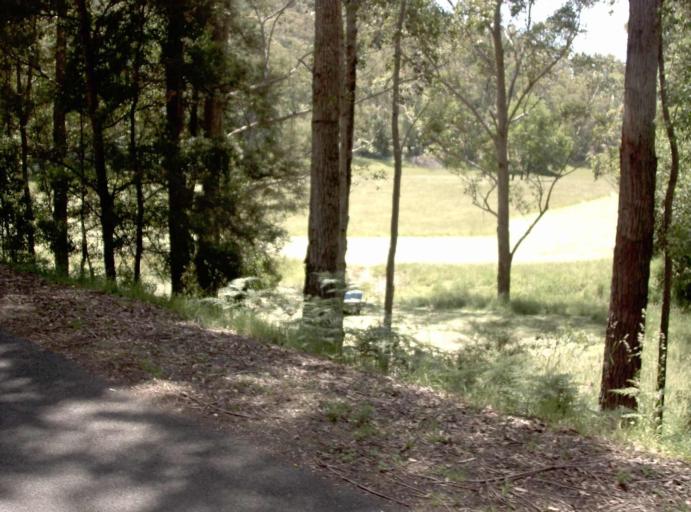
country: AU
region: New South Wales
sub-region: Bombala
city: Bombala
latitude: -37.5311
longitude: 148.9302
